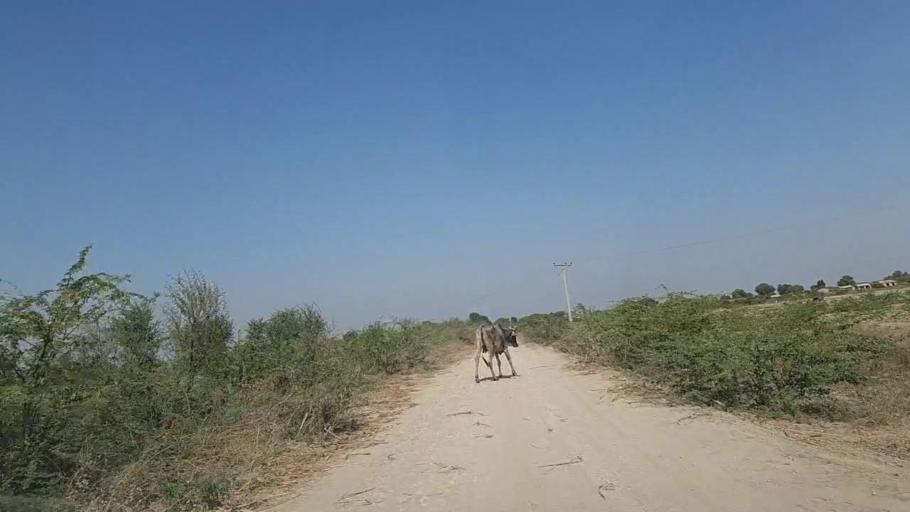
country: PK
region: Sindh
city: Samaro
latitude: 25.1793
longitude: 69.4040
